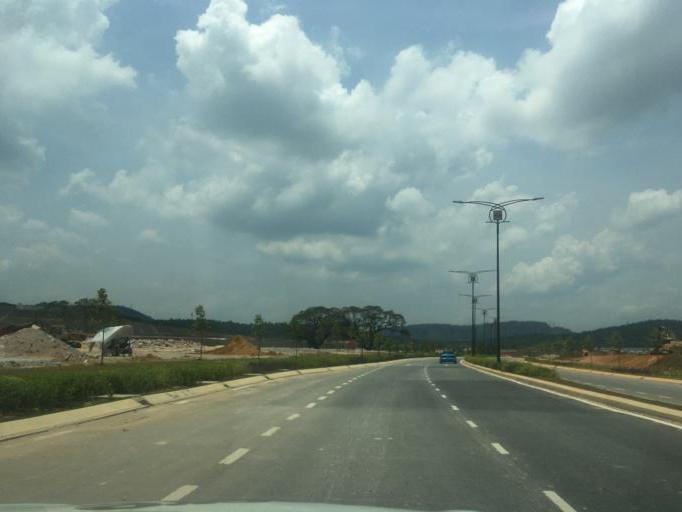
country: MY
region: Putrajaya
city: Putrajaya
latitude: 2.8454
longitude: 101.7028
